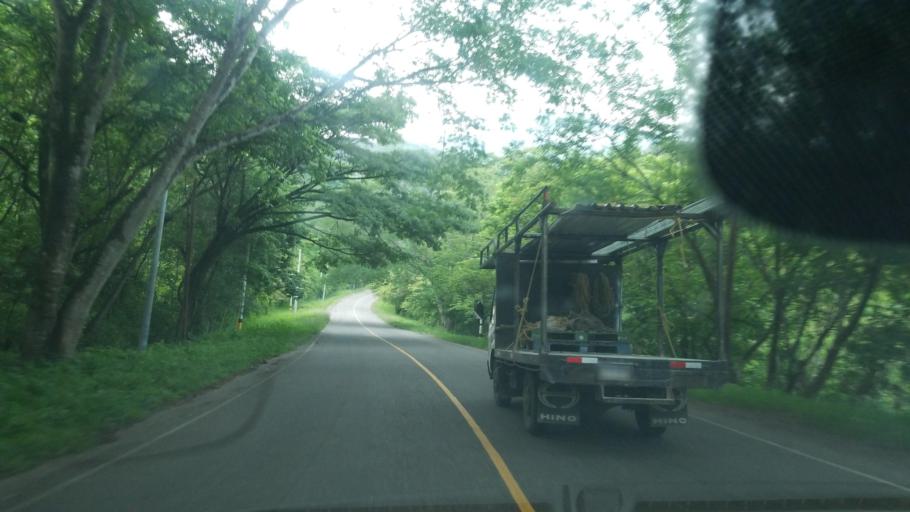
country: HN
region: Santa Barbara
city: Ceguaca
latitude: 14.8087
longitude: -88.1856
